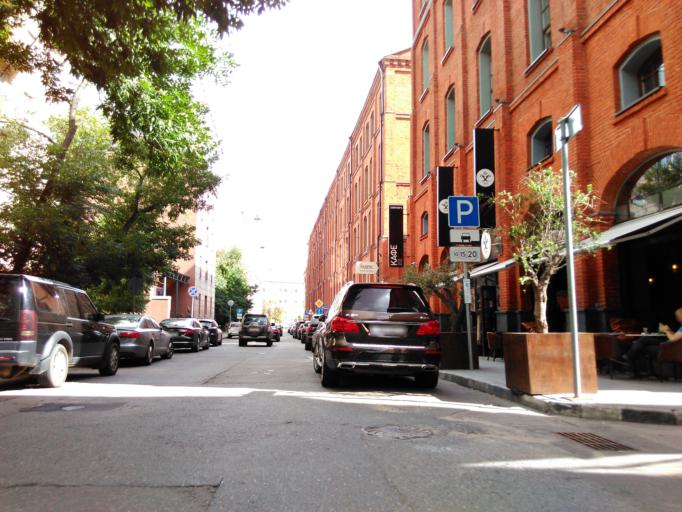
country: RU
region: Moskovskaya
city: Dorogomilovo
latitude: 55.7344
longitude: 37.5892
